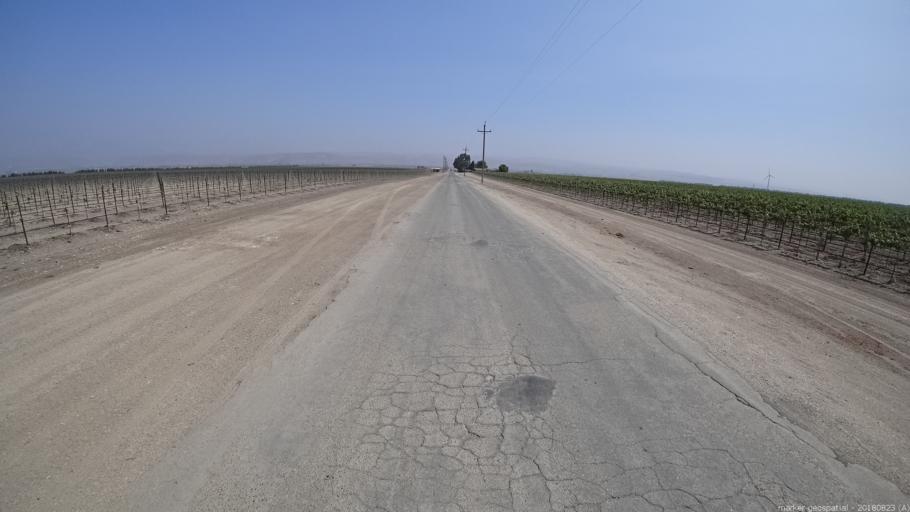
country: US
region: California
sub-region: Monterey County
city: Greenfield
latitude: 36.2781
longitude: -121.2131
